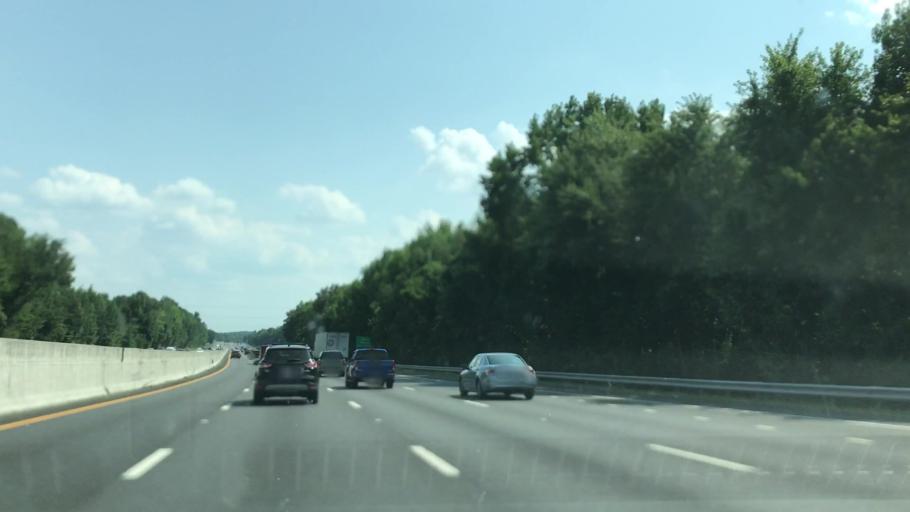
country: US
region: South Carolina
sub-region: York County
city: Fort Mill
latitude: 35.0225
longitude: -80.9681
